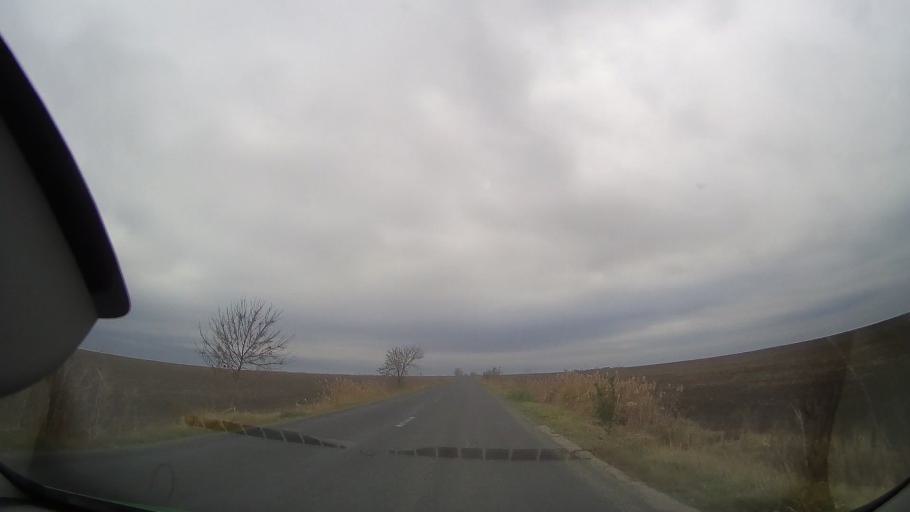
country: RO
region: Buzau
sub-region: Comuna Padina
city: Padina
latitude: 44.8021
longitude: 27.1341
